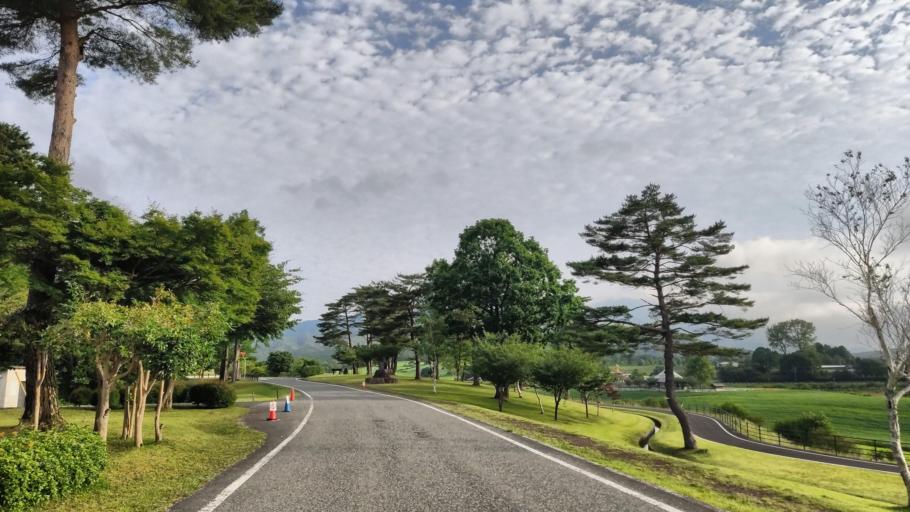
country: JP
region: Tottori
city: Kurayoshi
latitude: 35.2954
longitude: 133.6305
